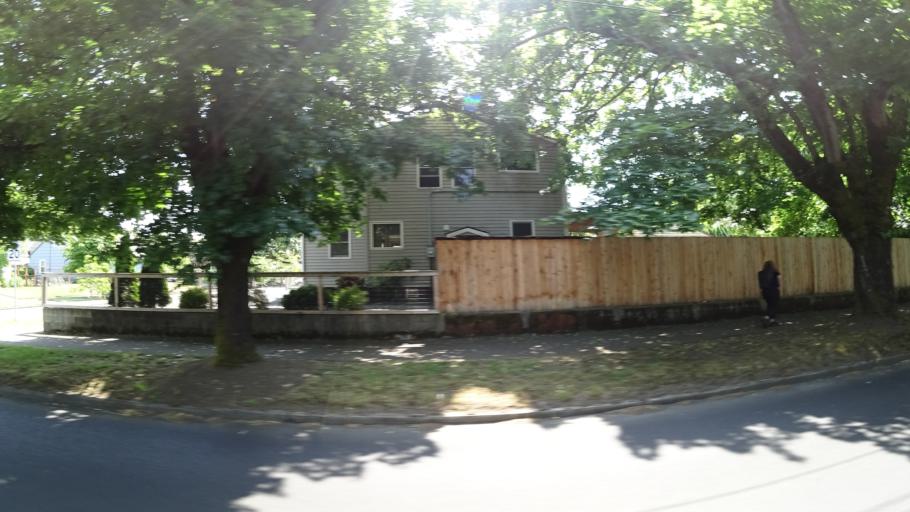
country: US
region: Oregon
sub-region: Multnomah County
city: Portland
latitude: 45.5771
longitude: -122.7062
